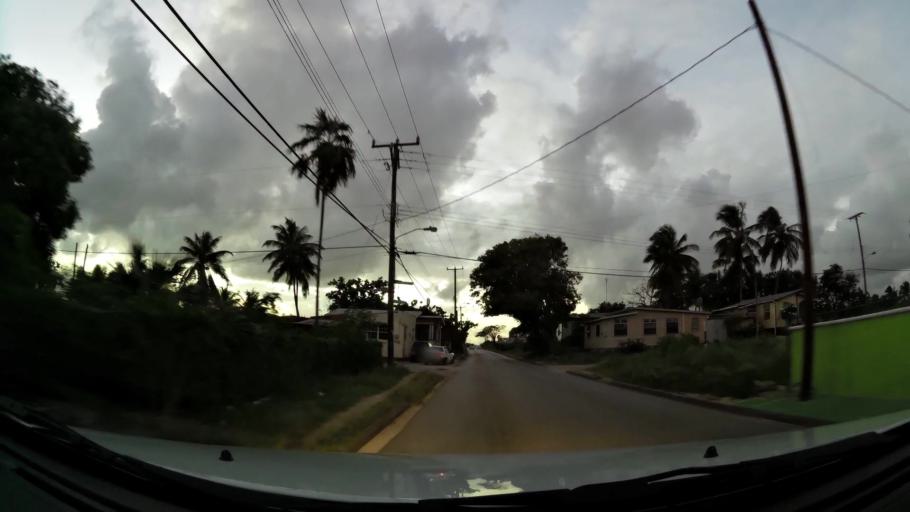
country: BB
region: Saint Philip
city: Crane
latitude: 13.1184
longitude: -59.4817
